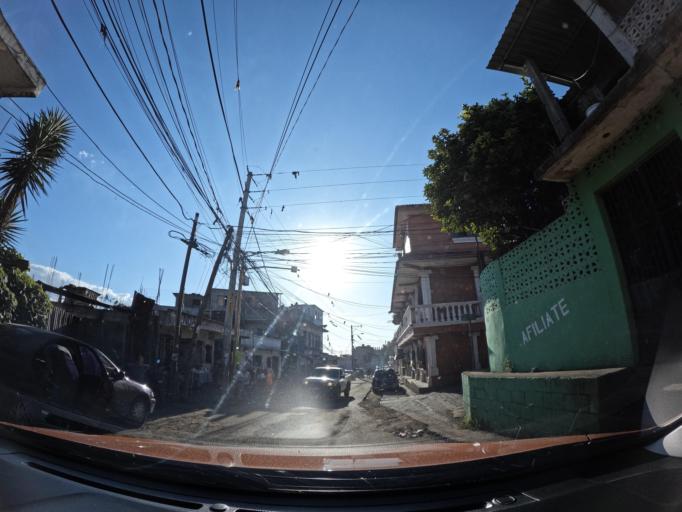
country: GT
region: Escuintla
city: Palin
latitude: 14.4080
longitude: -90.6944
